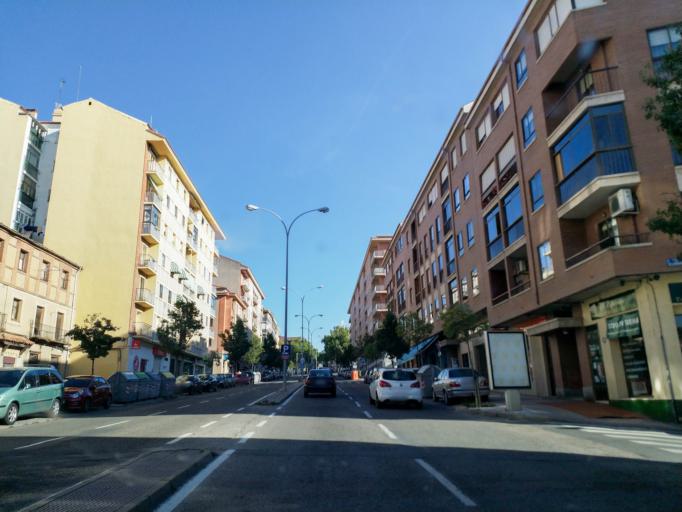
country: ES
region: Castille and Leon
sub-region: Provincia de Segovia
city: Segovia
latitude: 40.9460
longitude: -4.1229
